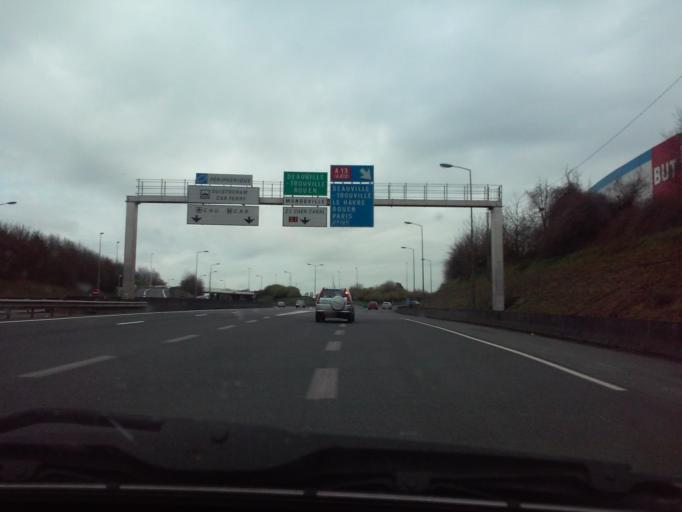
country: FR
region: Lower Normandy
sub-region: Departement du Calvados
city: Mondeville
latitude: 49.1662
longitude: -0.3038
